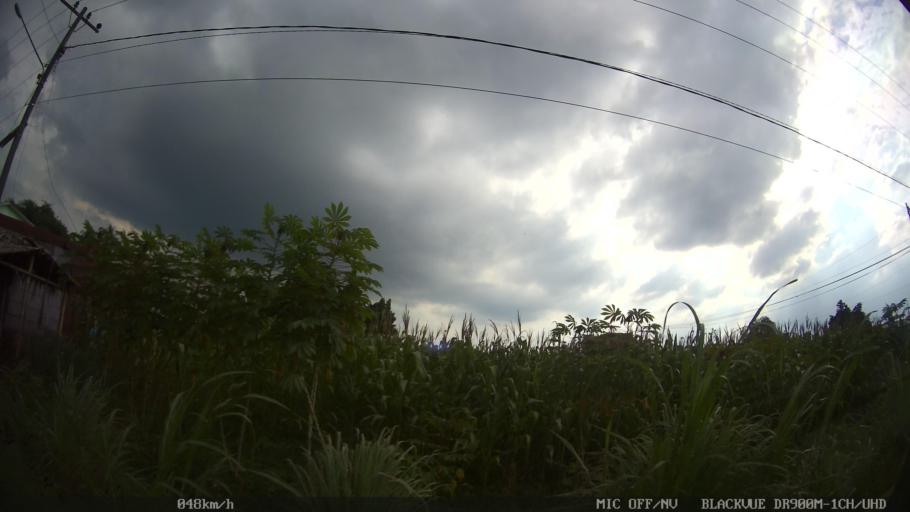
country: ID
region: North Sumatra
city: Sunggal
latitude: 3.5298
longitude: 98.6072
